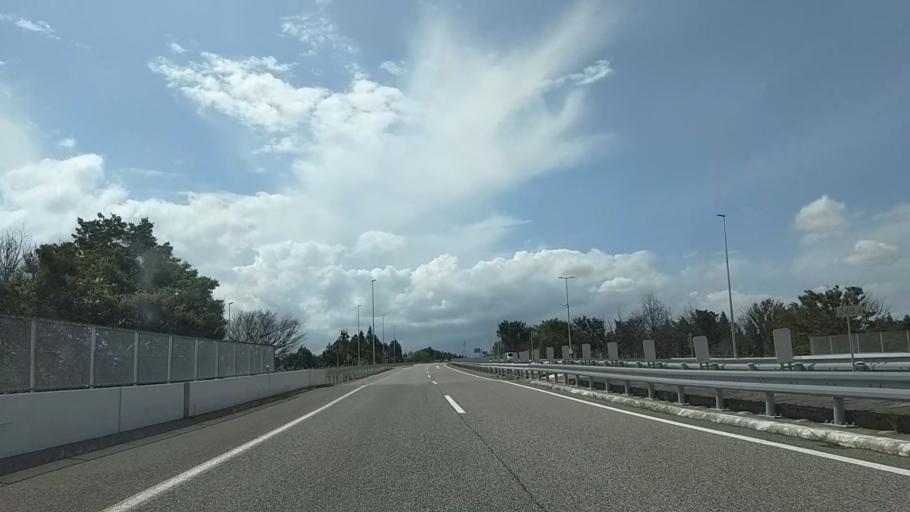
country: JP
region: Toyama
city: Kamiichi
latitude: 36.6857
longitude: 137.3256
